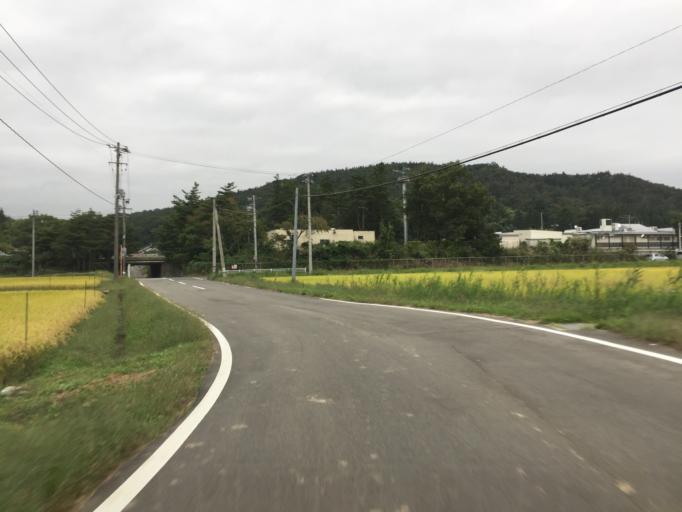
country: JP
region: Fukushima
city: Nihommatsu
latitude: 37.6601
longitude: 140.4446
